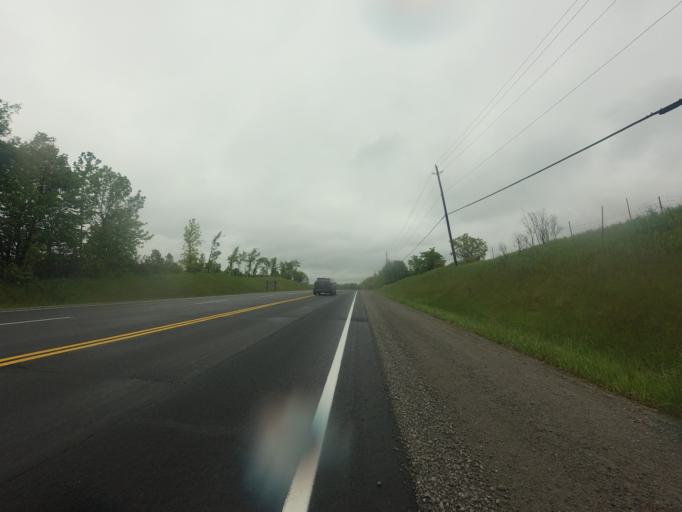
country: CA
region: Ontario
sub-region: Lanark County
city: Smiths Falls
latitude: 44.7589
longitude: -76.1232
